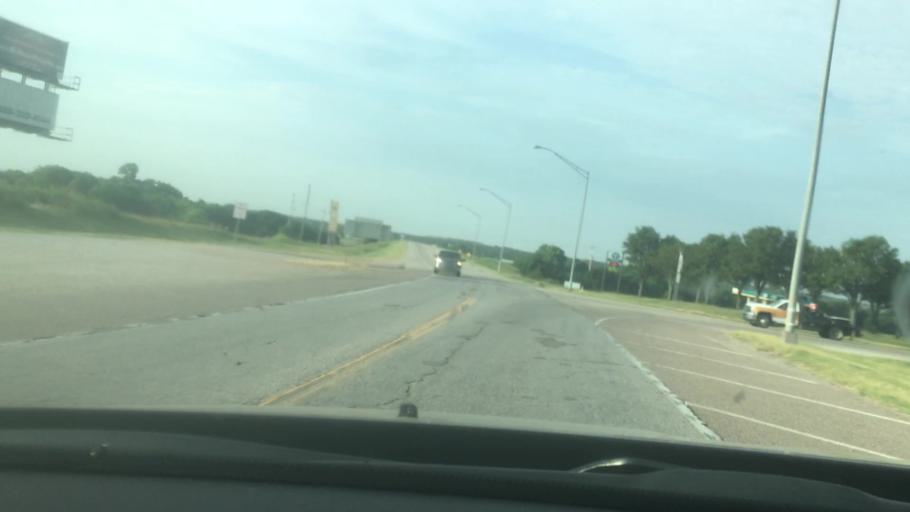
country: US
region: Oklahoma
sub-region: Pontotoc County
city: Ada
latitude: 34.6574
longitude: -96.7953
